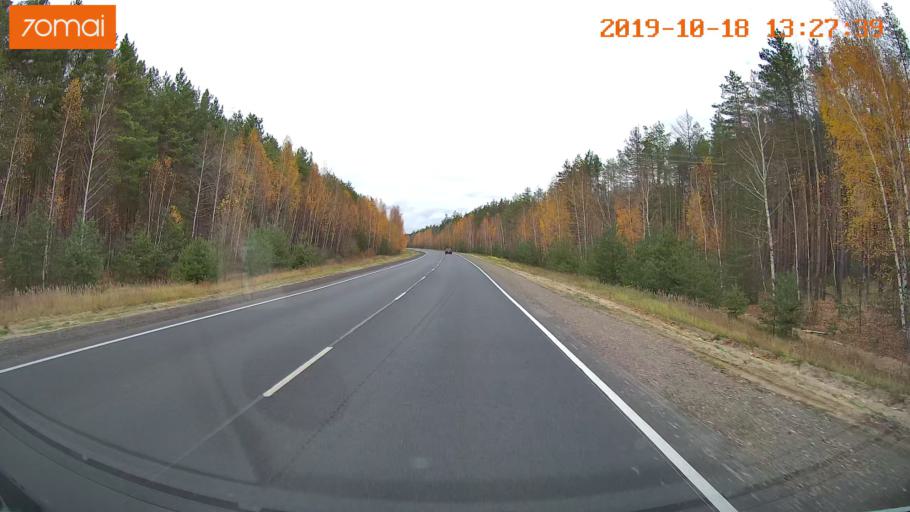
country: RU
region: Rjazan
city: Solotcha
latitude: 54.7667
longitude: 39.8575
